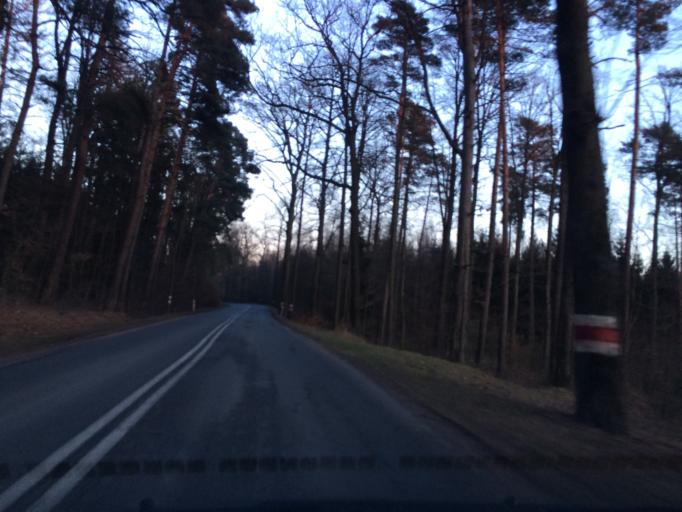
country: PL
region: Lower Silesian Voivodeship
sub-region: Powiat lwowecki
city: Lwowek Slaski
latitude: 51.1167
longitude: 15.6624
